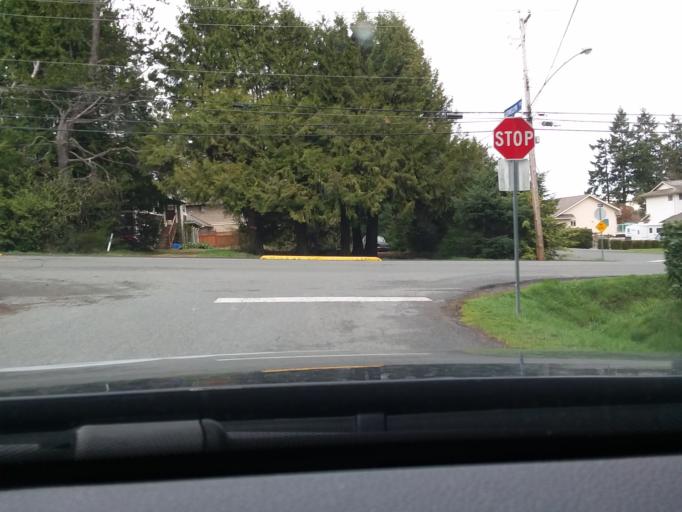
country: CA
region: British Columbia
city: North Saanich
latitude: 48.6173
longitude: -123.4204
